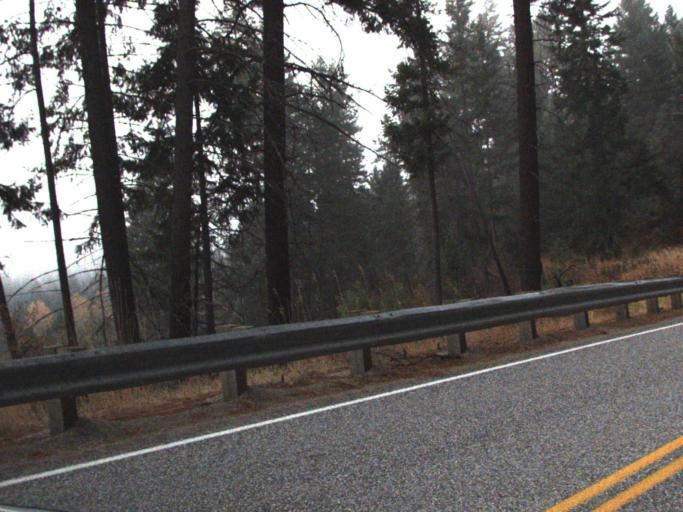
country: CA
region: British Columbia
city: Grand Forks
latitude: 48.8924
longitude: -118.2189
